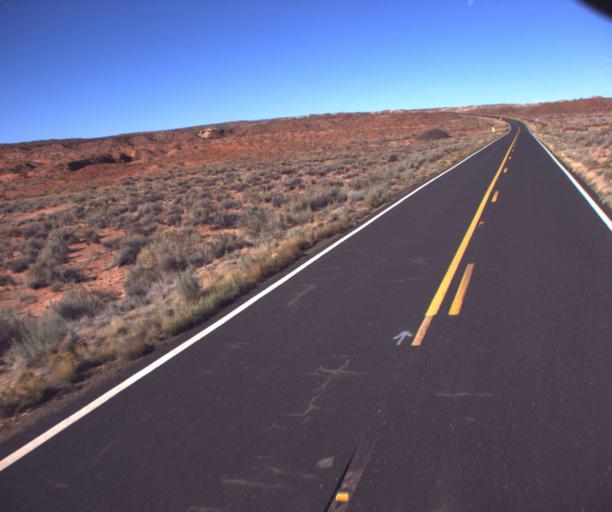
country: US
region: Arizona
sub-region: Coconino County
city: Page
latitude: 36.6886
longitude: -111.8738
